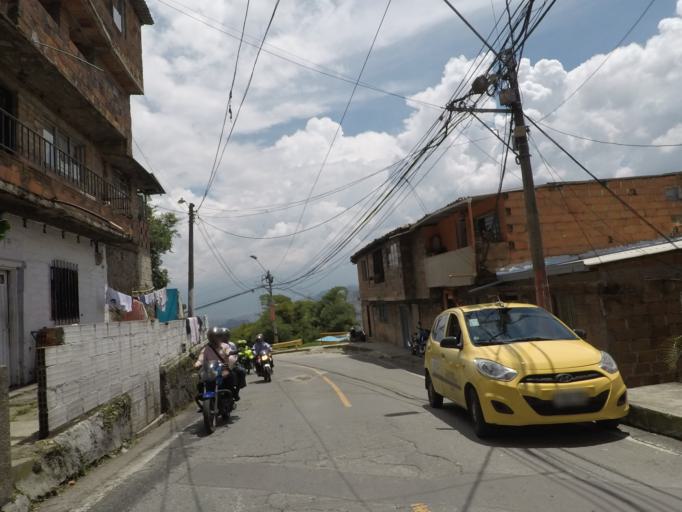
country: CO
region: Antioquia
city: Medellin
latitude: 6.2700
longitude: -75.6303
